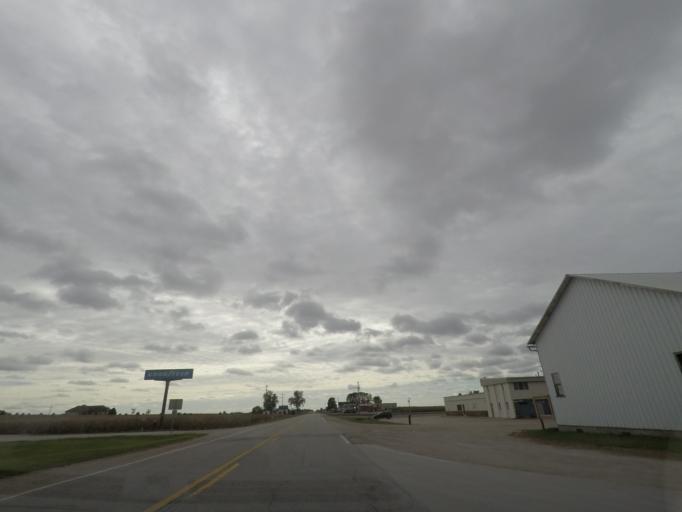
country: US
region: Iowa
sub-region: Story County
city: Nevada
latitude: 42.0174
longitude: -93.3095
